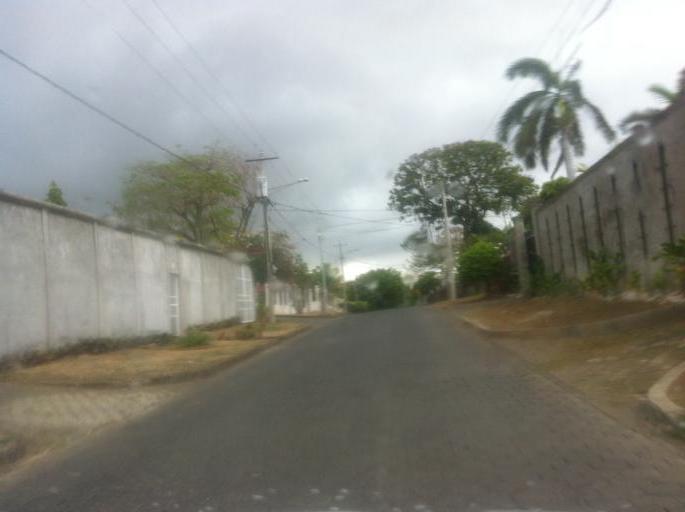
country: NI
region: Managua
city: Managua
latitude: 12.0997
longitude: -86.2354
